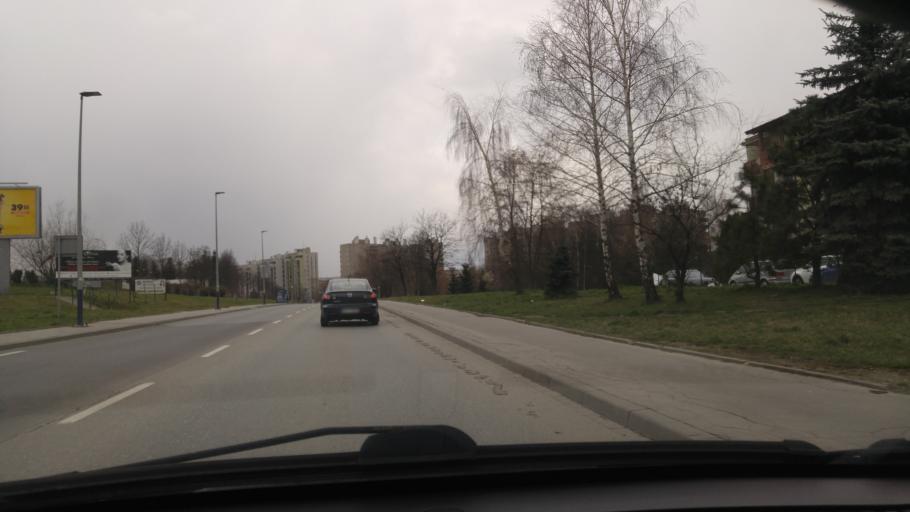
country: PL
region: Lesser Poland Voivodeship
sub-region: Powiat krakowski
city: Michalowice
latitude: 50.0946
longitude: 20.0230
